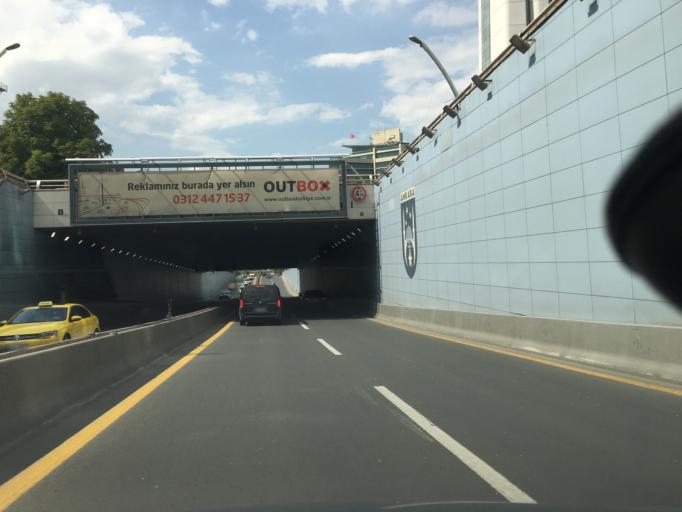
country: TR
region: Ankara
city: Cankaya
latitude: 39.9082
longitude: 32.8568
